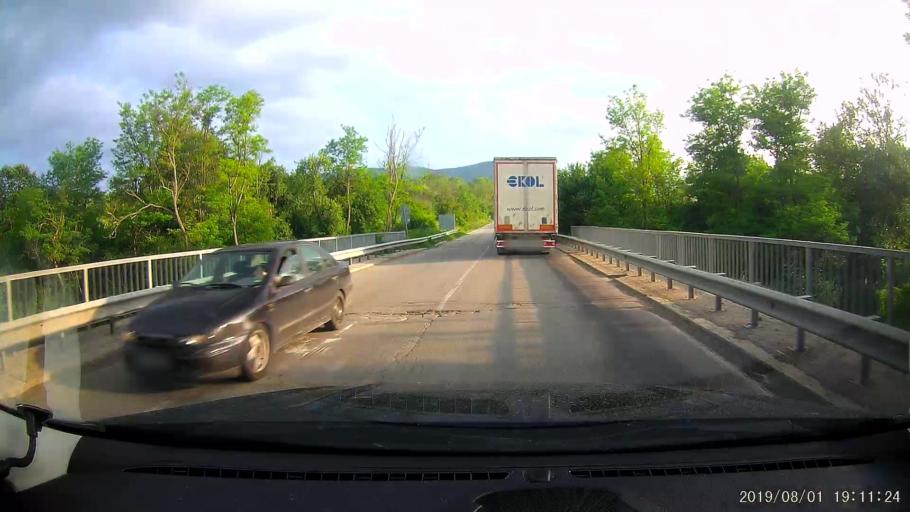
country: BG
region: Shumen
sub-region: Obshtina Smyadovo
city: Smyadovo
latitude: 42.9753
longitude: 26.9615
